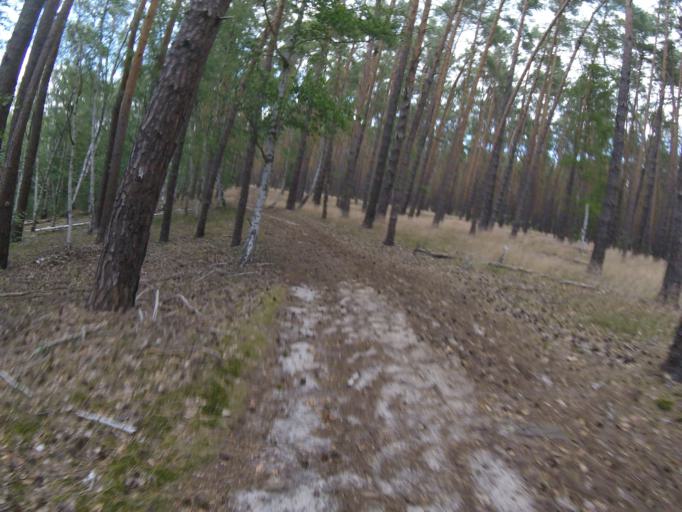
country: DE
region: Brandenburg
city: Gross Koris
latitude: 52.2028
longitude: 13.6390
